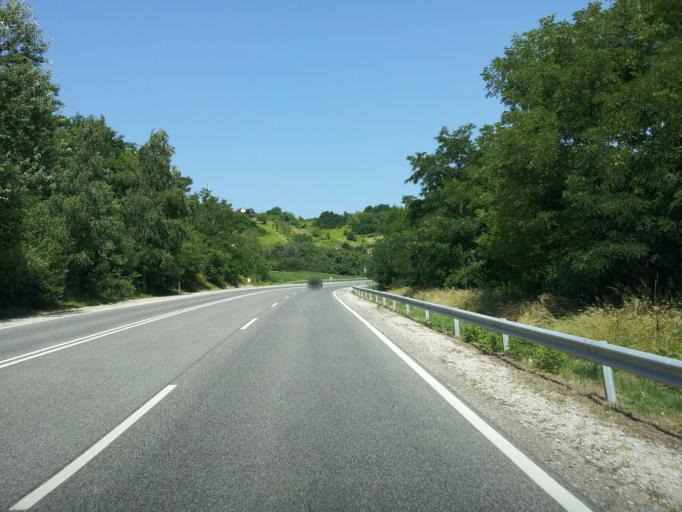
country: HU
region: Zala
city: Pacsa
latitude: 46.8242
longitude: 16.9731
